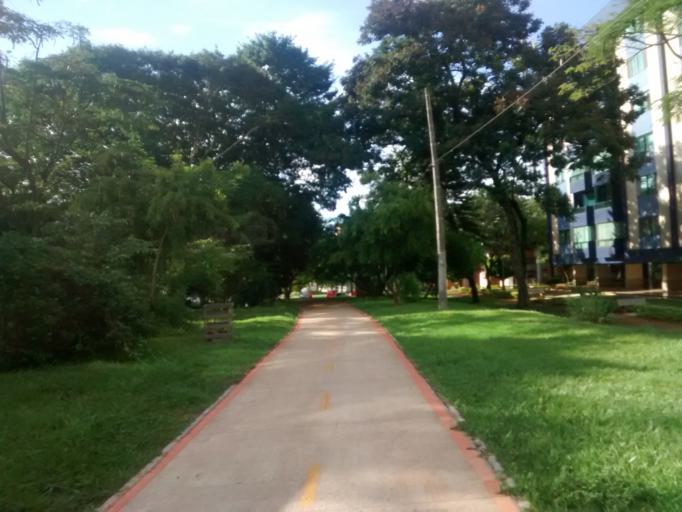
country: BR
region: Federal District
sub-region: Brasilia
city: Brasilia
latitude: -15.7384
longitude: -47.8952
